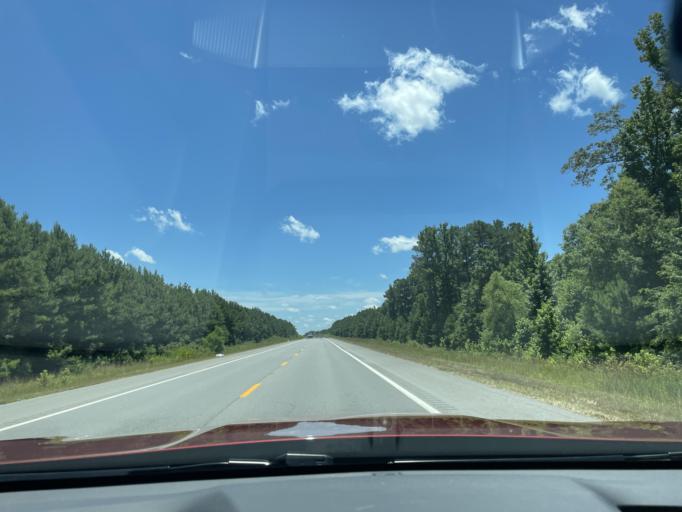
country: US
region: Arkansas
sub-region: Lincoln County
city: Star City
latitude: 33.9658
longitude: -91.9121
